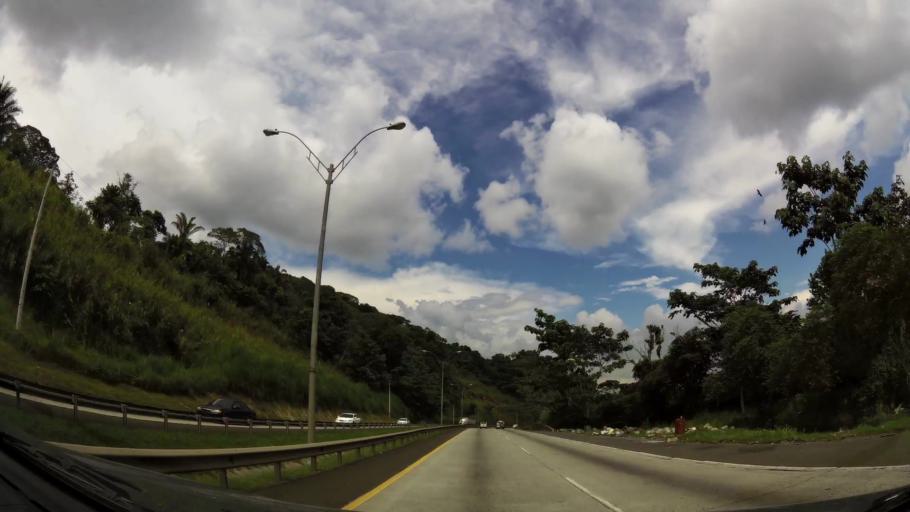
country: PA
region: Panama
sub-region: Distrito de Panama
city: Paraiso
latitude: 9.0066
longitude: -79.6488
